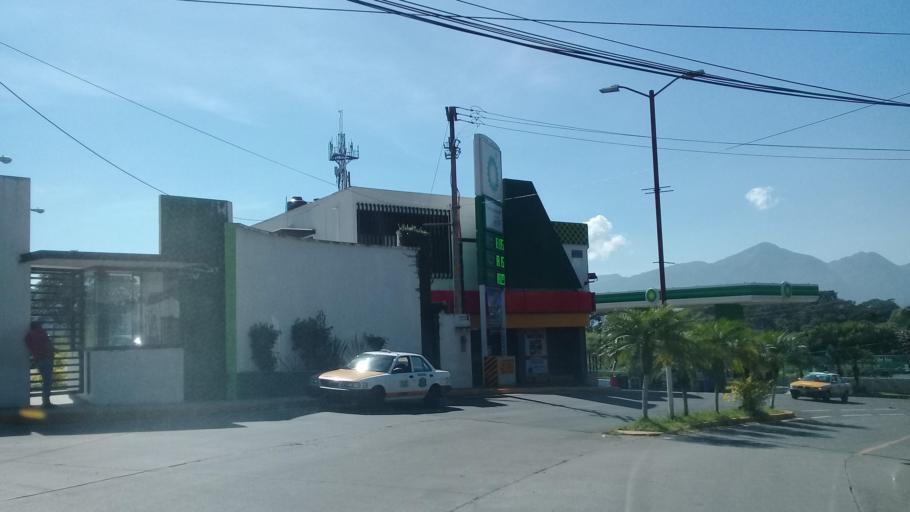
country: MX
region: Veracruz
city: Amatlan de los Reyes
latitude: 18.8537
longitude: -96.9121
